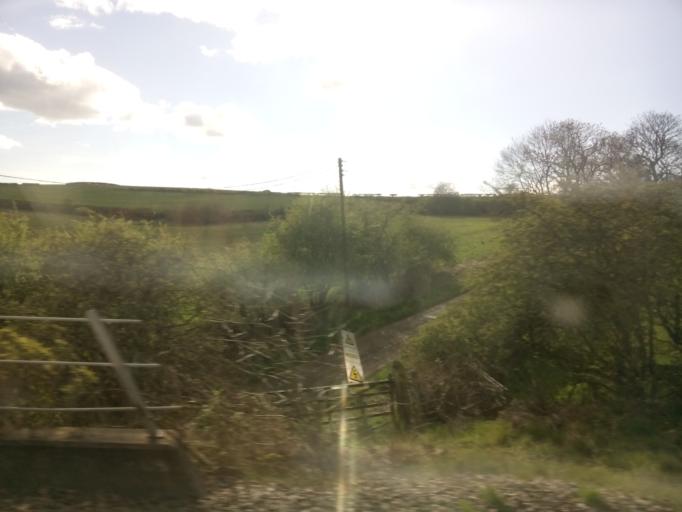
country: GB
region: England
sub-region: County Durham
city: Durham
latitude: 54.8169
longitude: -1.5755
